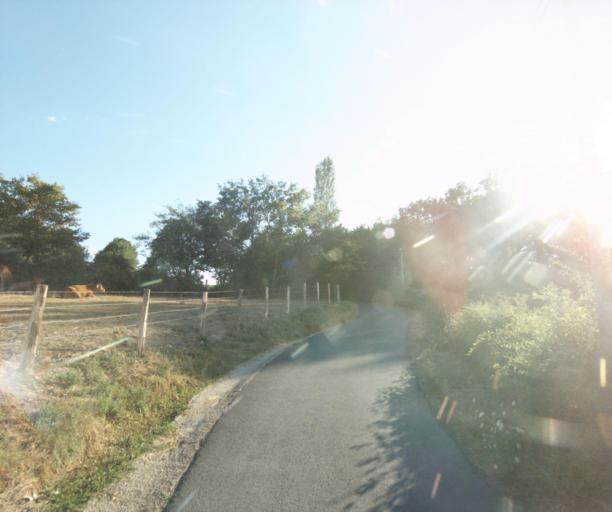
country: FR
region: Rhone-Alpes
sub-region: Departement du Rhone
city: Lozanne
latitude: 45.8461
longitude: 4.6871
